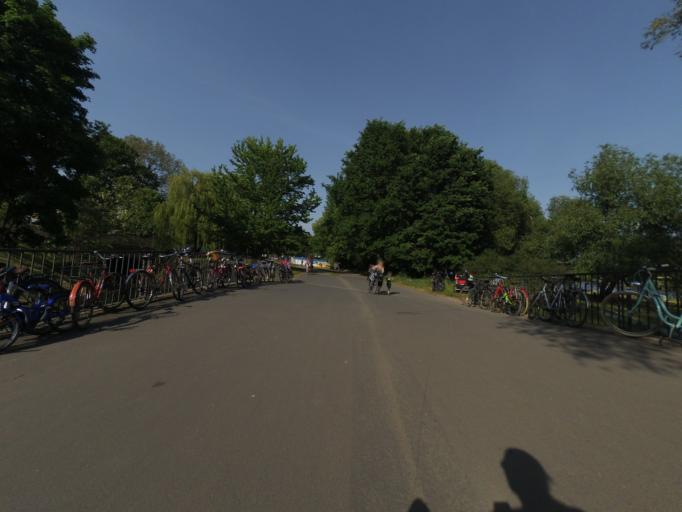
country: DE
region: Saxony
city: Albertstadt
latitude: 51.0622
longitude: 13.7623
